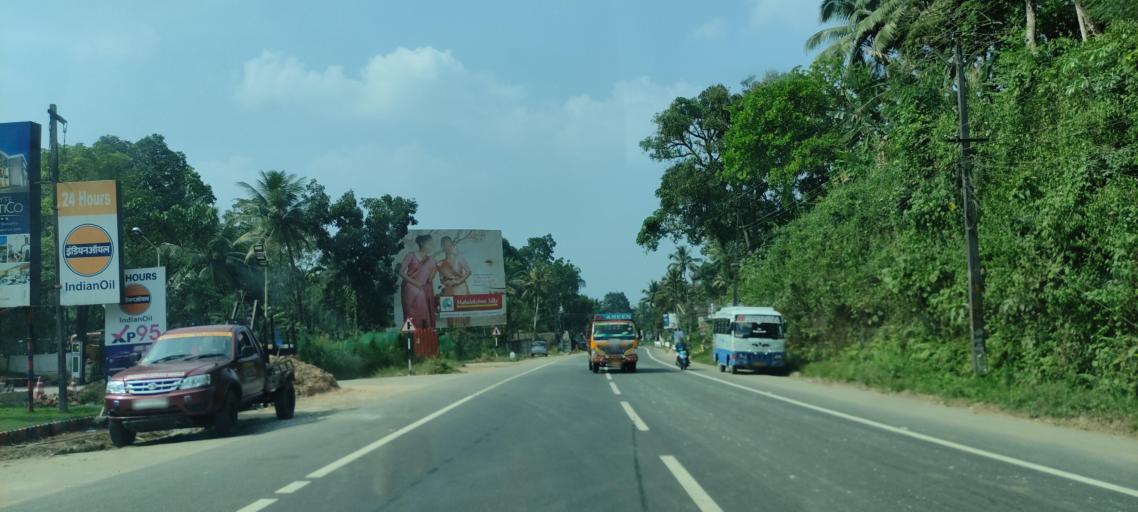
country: IN
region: Kerala
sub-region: Pattanamtitta
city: Adur
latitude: 9.1664
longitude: 76.7183
